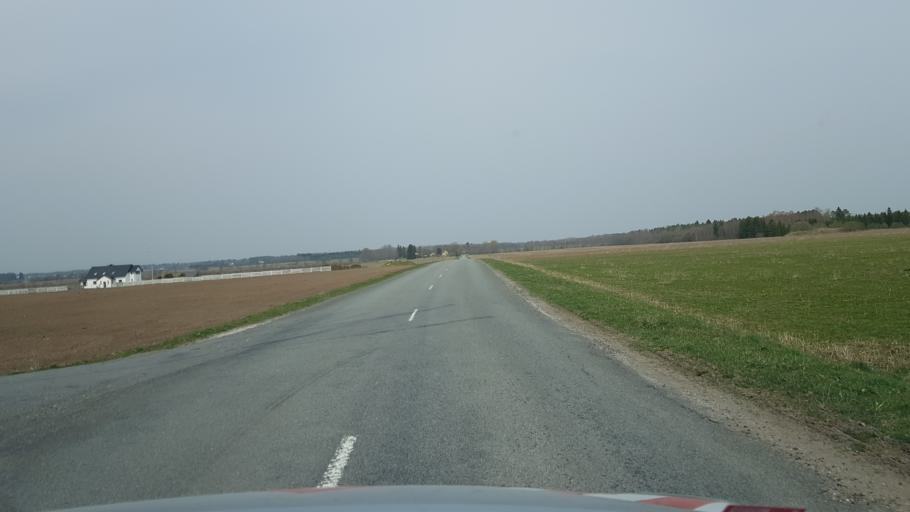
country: EE
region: Harju
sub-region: Kiili vald
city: Kiili
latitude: 59.2758
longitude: 24.8745
